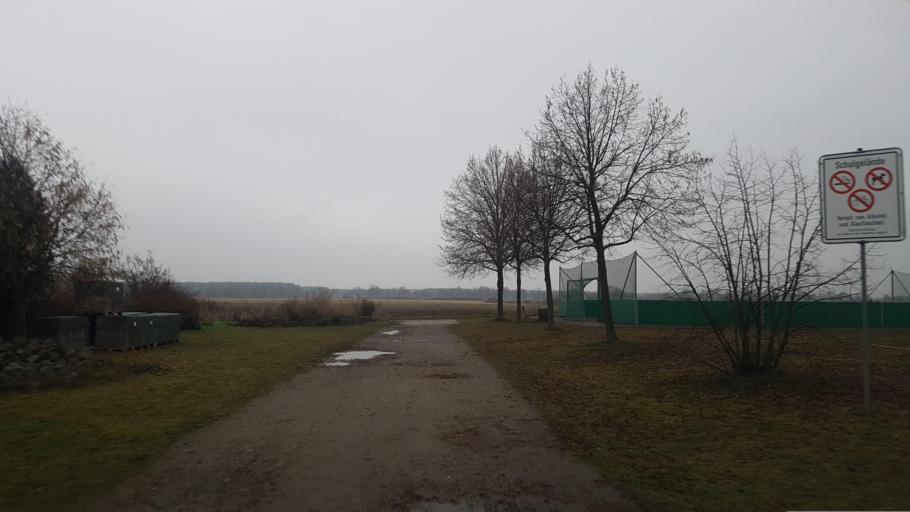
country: DE
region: Brandenburg
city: Vetschau
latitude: 51.7274
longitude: 14.0415
